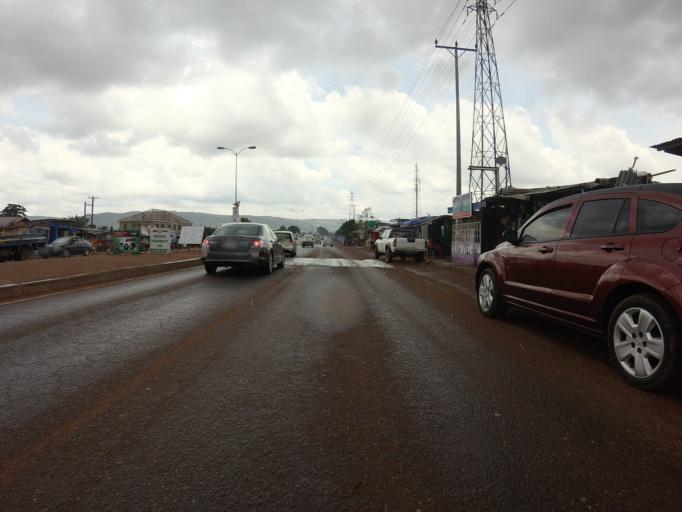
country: GH
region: Greater Accra
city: Medina Estates
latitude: 5.7433
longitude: -0.1768
